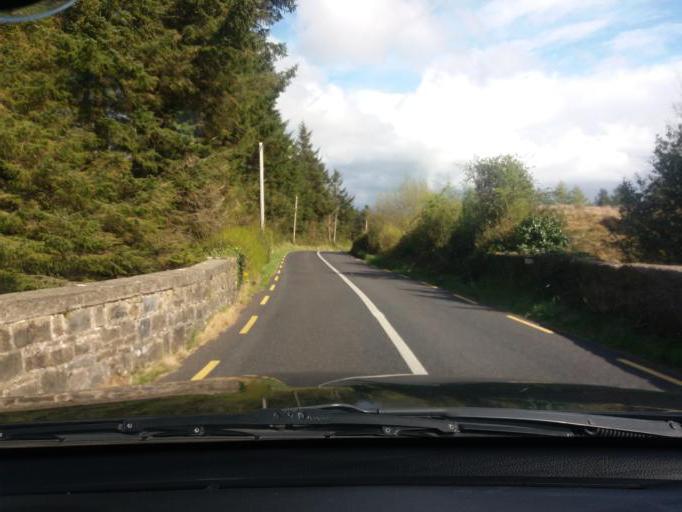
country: IE
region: Connaught
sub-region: County Leitrim
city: Kinlough
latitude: 54.3724
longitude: -8.2746
